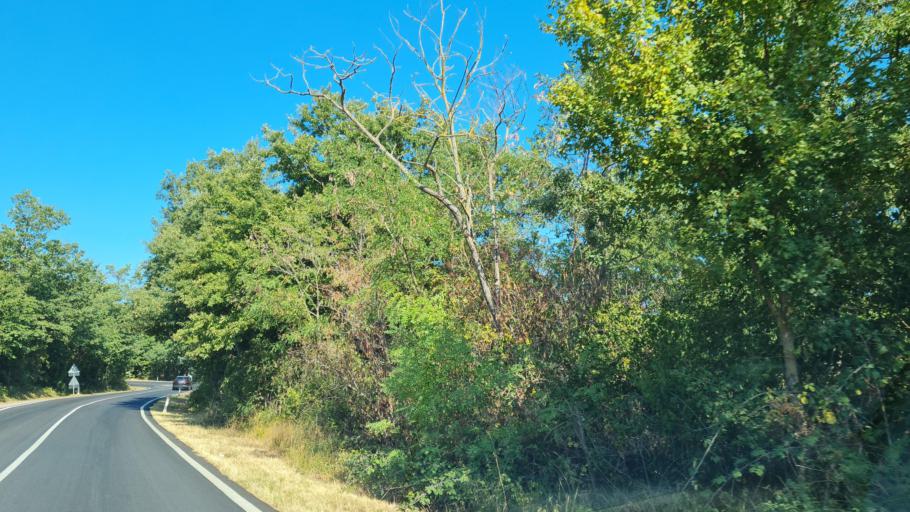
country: IT
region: Tuscany
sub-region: Provincia di Siena
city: Chianciano Terme
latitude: 43.0408
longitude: 11.8053
